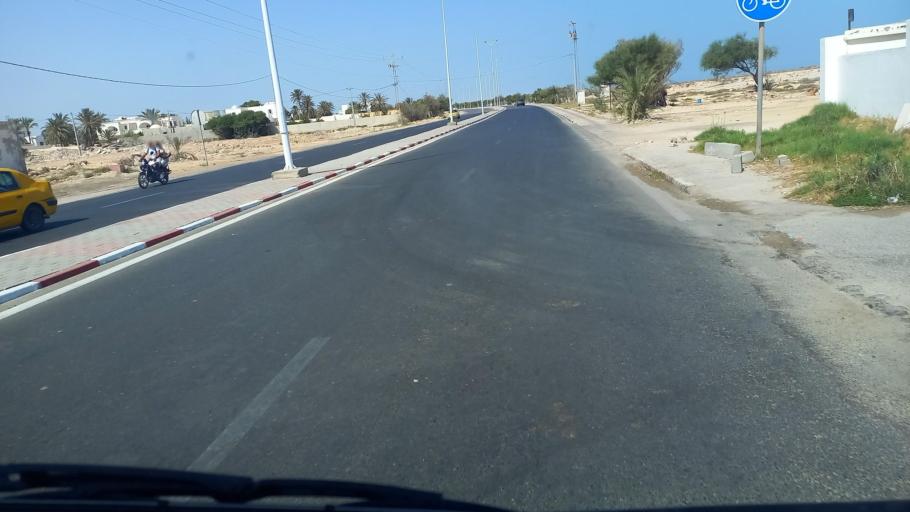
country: TN
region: Madanin
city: Midoun
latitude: 33.8690
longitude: 10.9559
